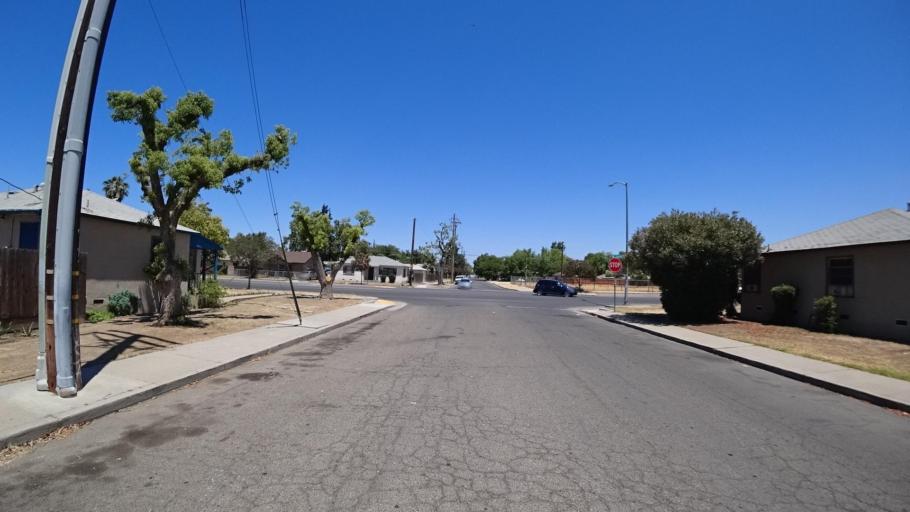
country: US
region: California
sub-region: Fresno County
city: Fresno
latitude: 36.7792
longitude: -119.7951
